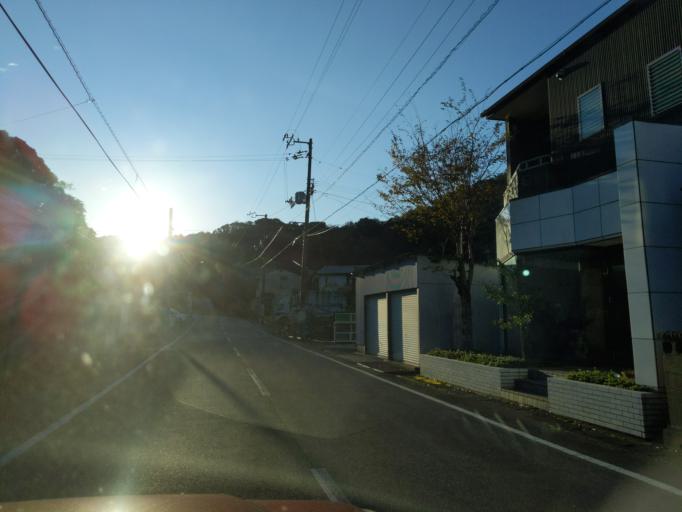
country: JP
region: Kochi
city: Muroto-misakicho
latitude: 33.5439
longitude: 134.2970
